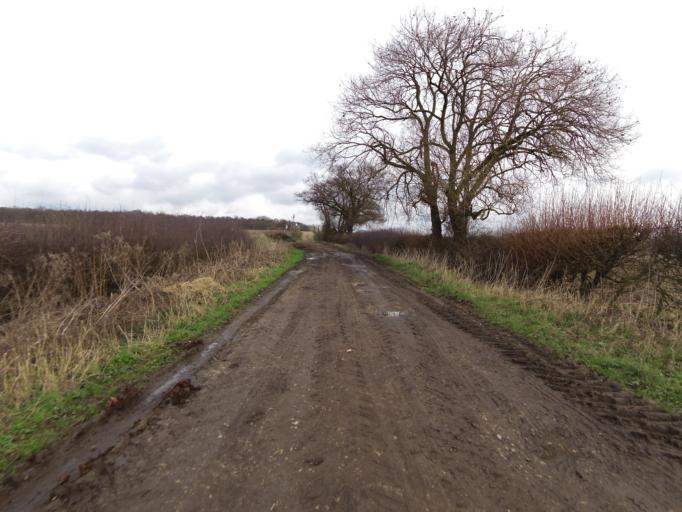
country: GB
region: England
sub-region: Doncaster
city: Askern
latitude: 53.5801
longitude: -1.1327
